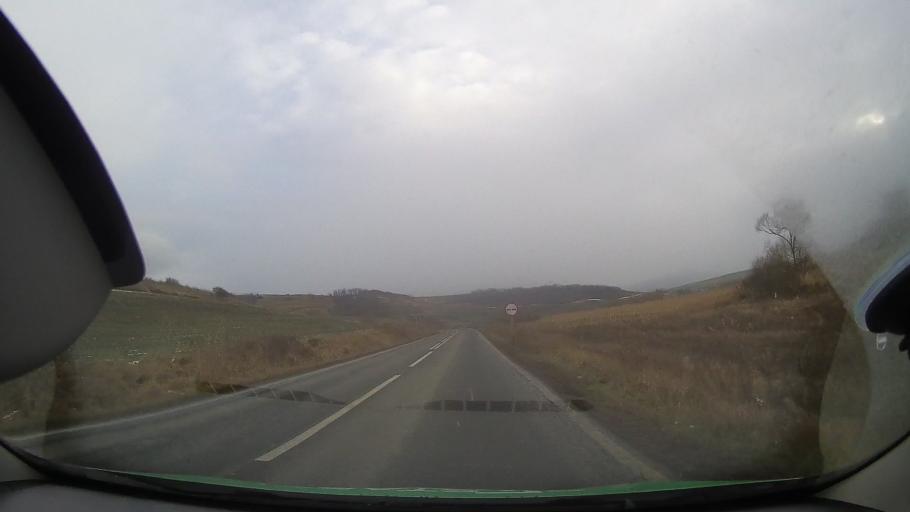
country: RO
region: Sibiu
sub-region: Comuna Blajel
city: Blajel
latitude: 46.2299
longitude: 24.3107
